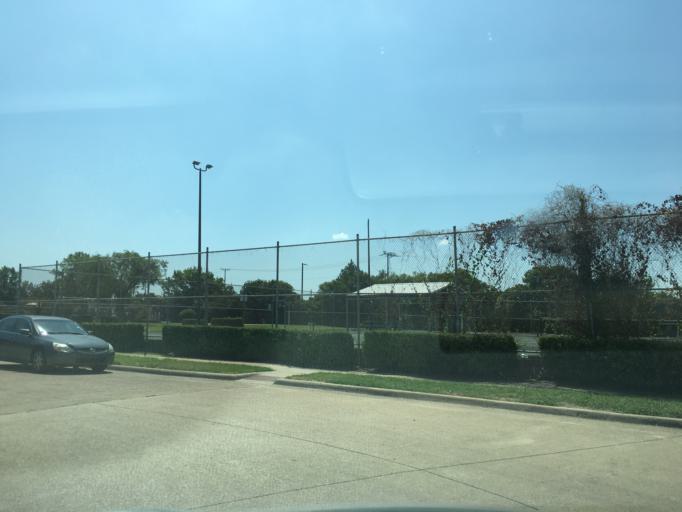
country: US
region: Texas
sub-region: Dallas County
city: Garland
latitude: 32.8670
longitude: -96.6592
